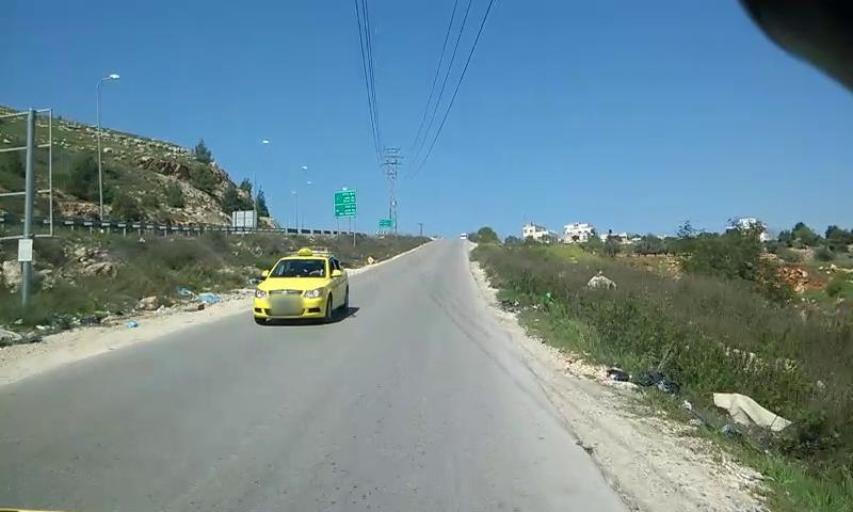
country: PS
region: West Bank
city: Al Khadir
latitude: 31.7064
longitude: 35.1551
